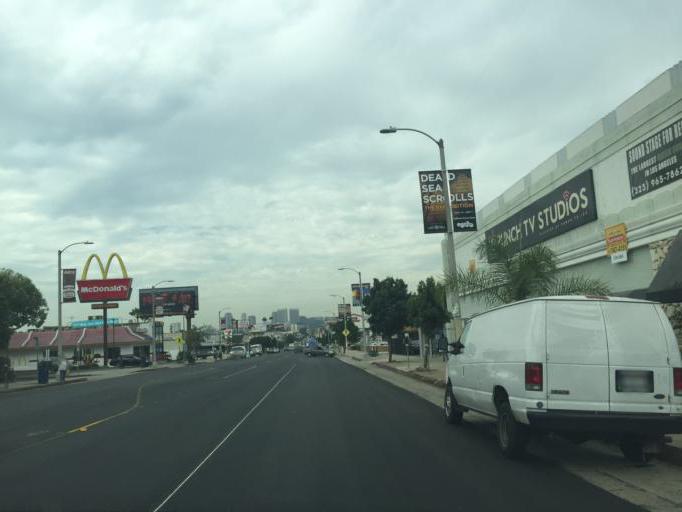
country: US
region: California
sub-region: Los Angeles County
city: West Hollywood
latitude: 34.0519
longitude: -118.3679
